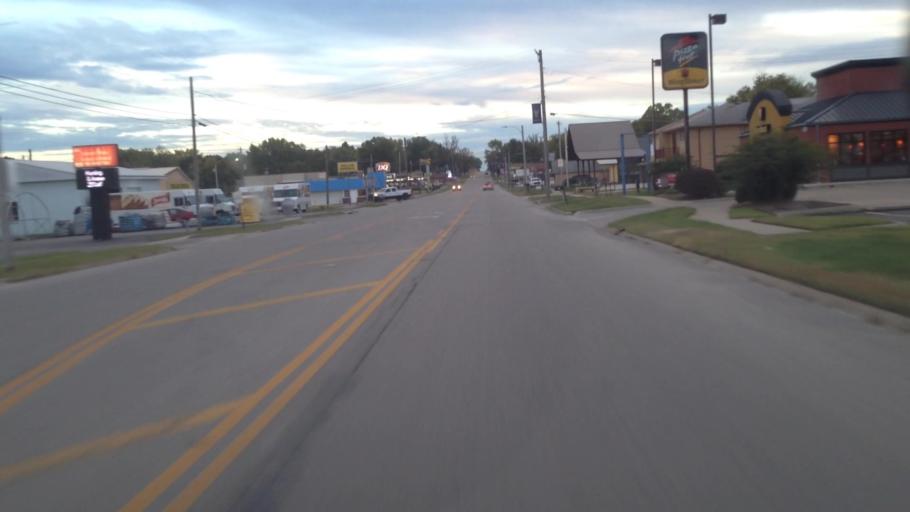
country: US
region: Kansas
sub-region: Anderson County
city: Garnett
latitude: 38.2876
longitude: -95.2493
